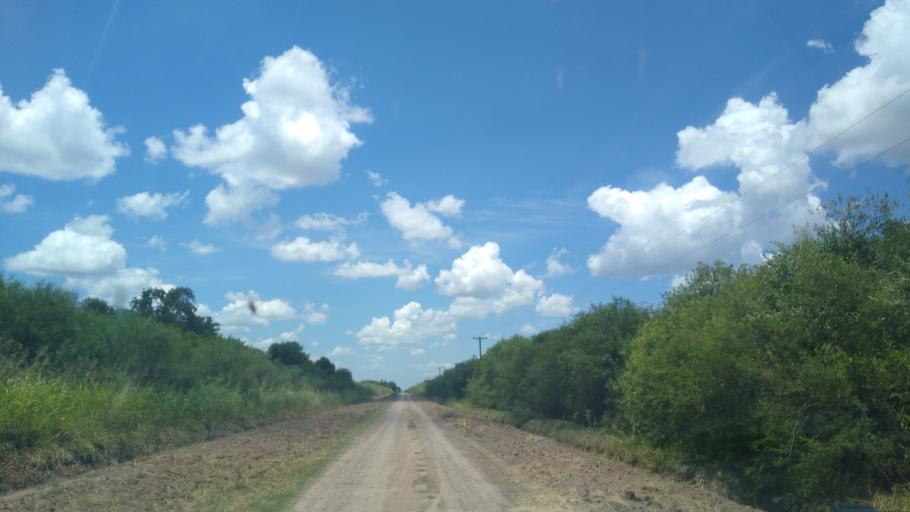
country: AR
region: Chaco
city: Presidencia Roque Saenz Pena
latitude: -26.7395
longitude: -60.3327
